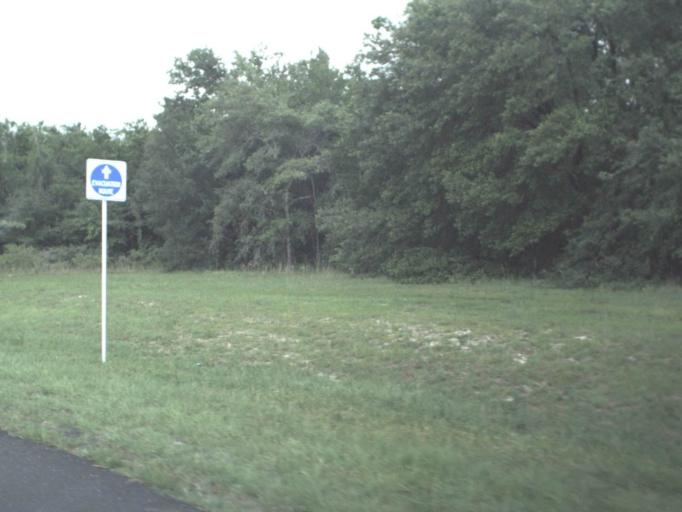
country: US
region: Florida
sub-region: Bradford County
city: Starke
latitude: 30.1086
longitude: -82.0501
